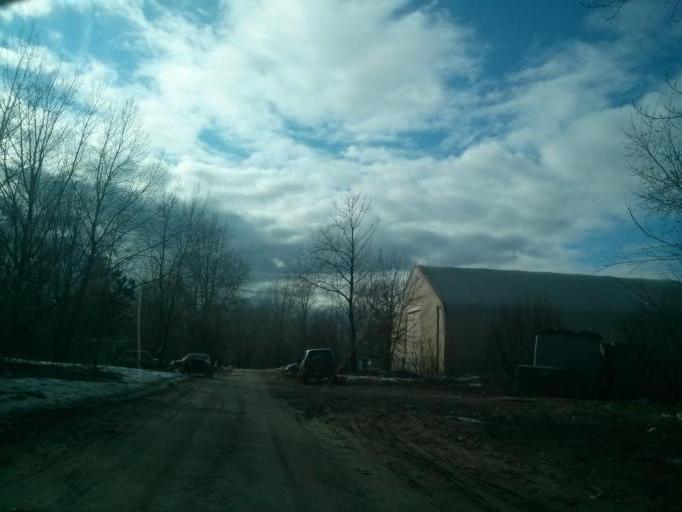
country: RU
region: Nizjnij Novgorod
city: Bor
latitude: 56.3292
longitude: 44.0563
